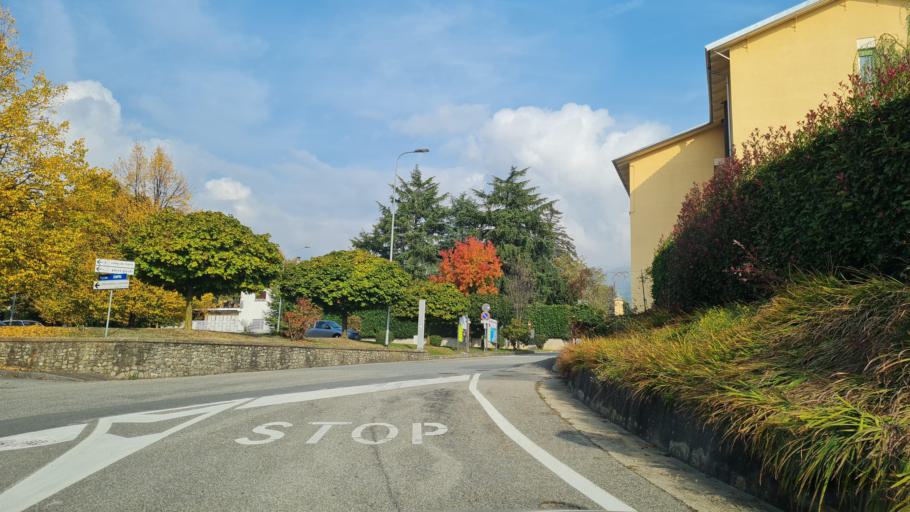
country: IT
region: Piedmont
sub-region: Provincia di Biella
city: Graglia
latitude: 45.5602
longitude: 7.9793
